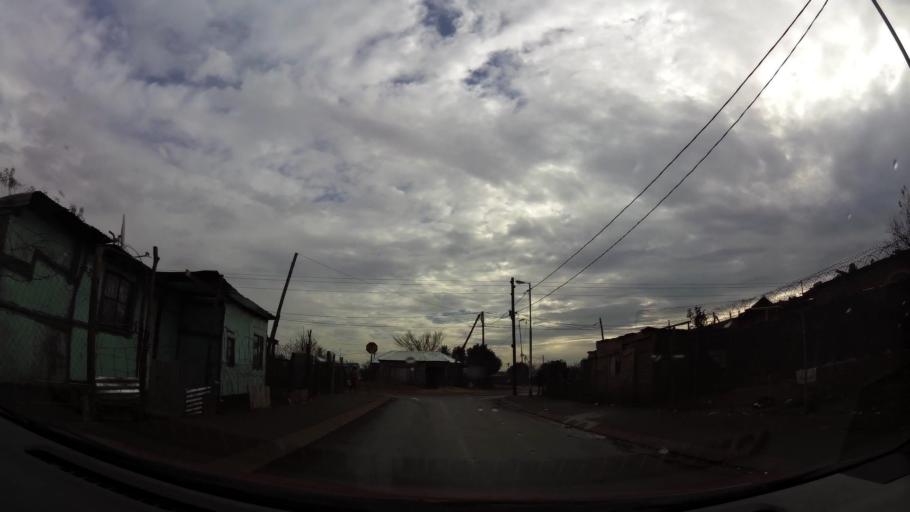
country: ZA
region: Gauteng
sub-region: City of Johannesburg Metropolitan Municipality
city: Soweto
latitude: -26.2852
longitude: 27.8418
